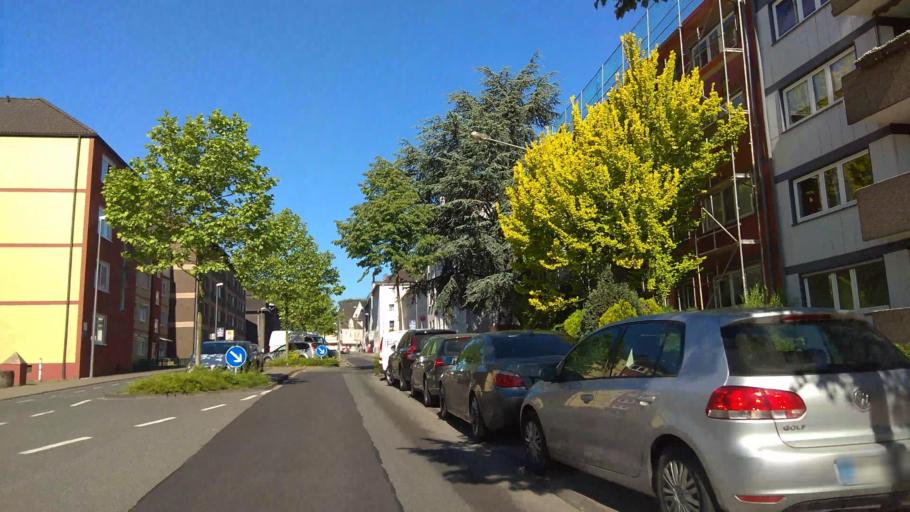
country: DE
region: North Rhine-Westphalia
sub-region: Regierungsbezirk Munster
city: Bottrop
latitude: 51.5123
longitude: 6.9373
